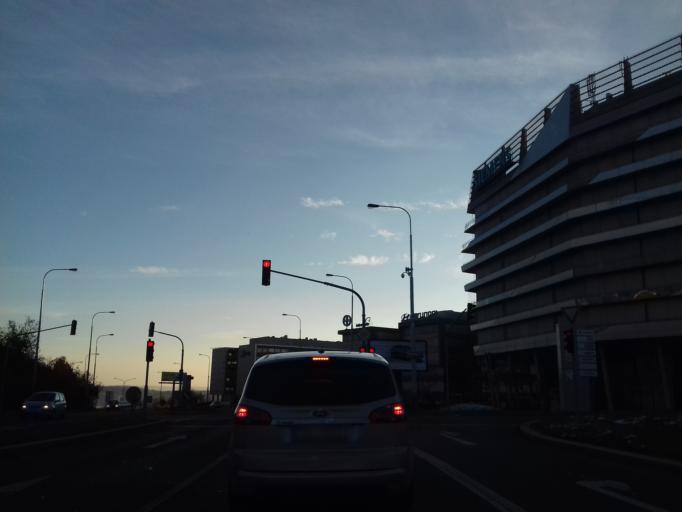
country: CZ
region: Central Bohemia
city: Hostivice
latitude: 50.0487
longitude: 14.3080
